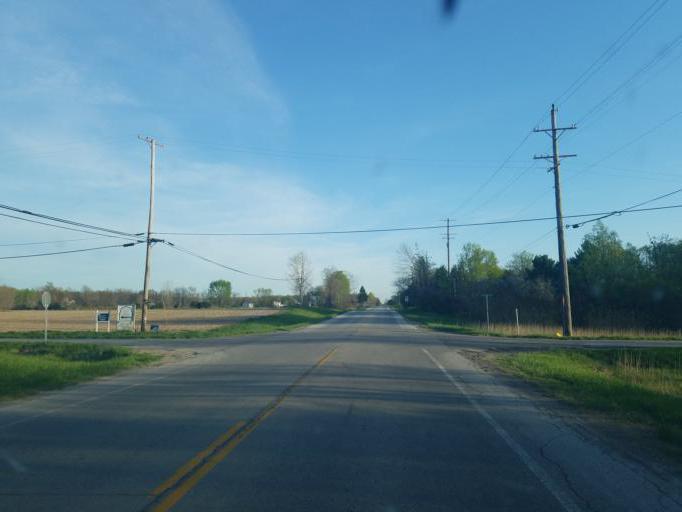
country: US
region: Ohio
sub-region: Ashtabula County
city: Conneaut
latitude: 41.8192
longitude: -80.5722
